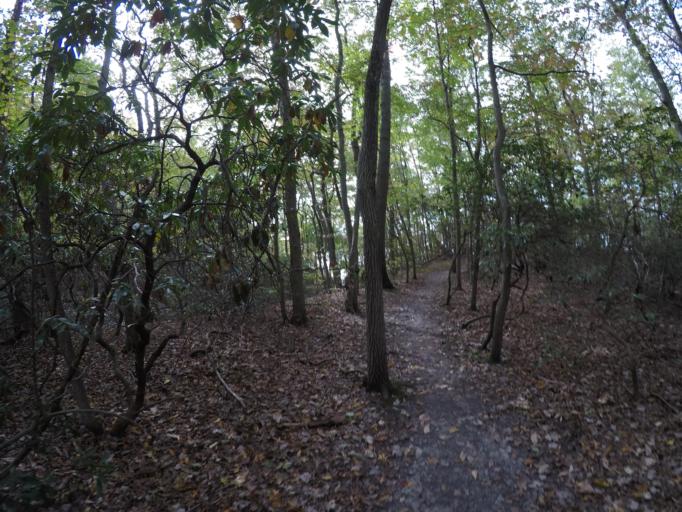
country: US
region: Maryland
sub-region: Harford County
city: Riverside
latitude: 39.4504
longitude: -76.2696
